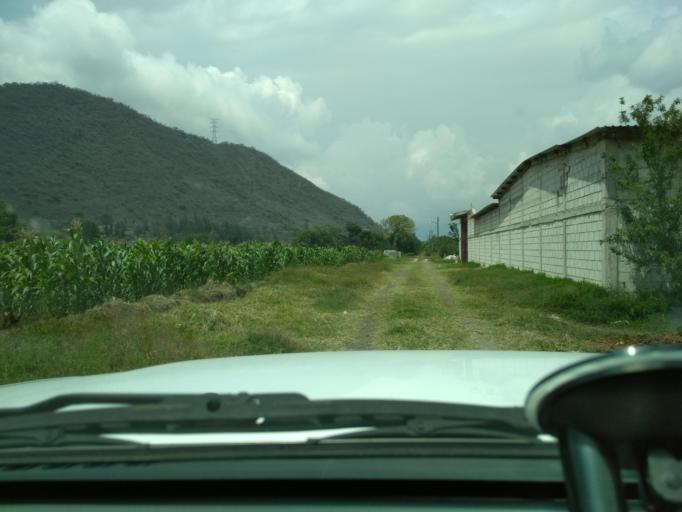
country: MX
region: Veracruz
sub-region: Nogales
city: Taza de Agua Ojo Zarco
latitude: 18.7788
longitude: -97.2180
